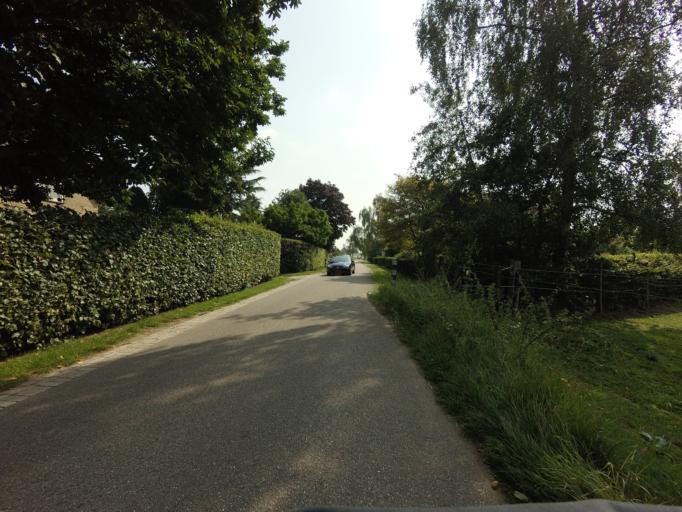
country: NL
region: Gelderland
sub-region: Gemeente Zevenaar
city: Zevenaar
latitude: 51.9050
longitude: 6.1503
